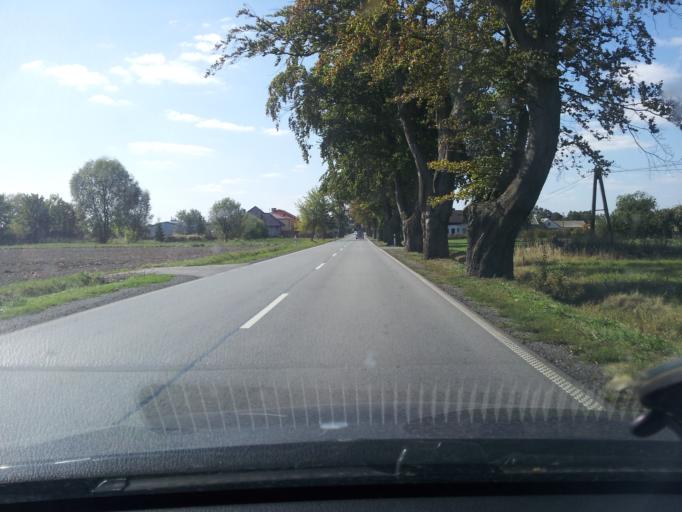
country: PL
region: Kujawsko-Pomorskie
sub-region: Powiat golubsko-dobrzynski
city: Radomin
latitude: 53.0862
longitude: 19.2046
